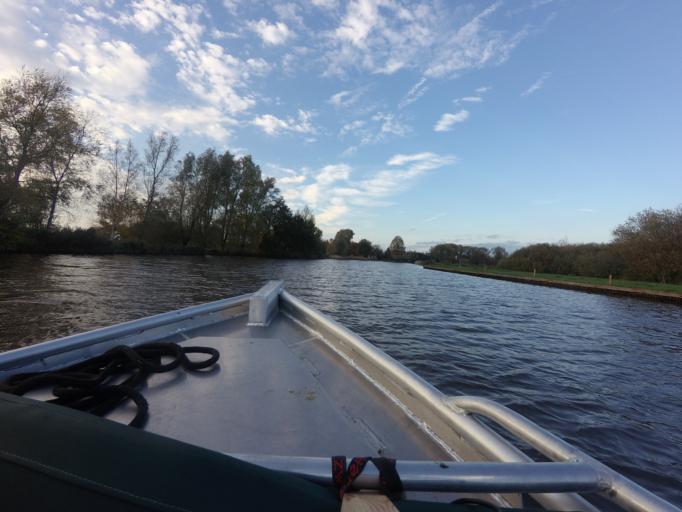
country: NL
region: Overijssel
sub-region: Gemeente Steenwijkerland
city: Blokzijl
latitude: 52.7393
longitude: 5.9937
